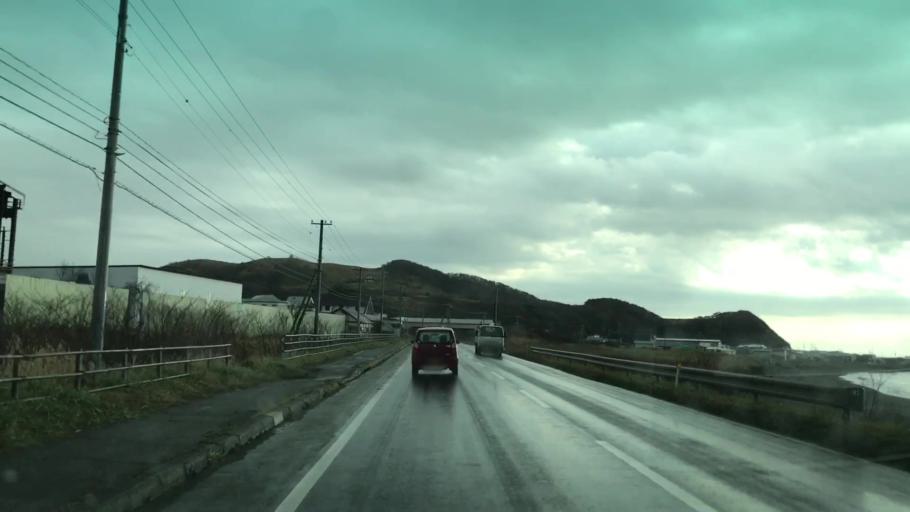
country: JP
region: Hokkaido
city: Shizunai-furukawacho
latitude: 42.1917
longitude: 142.6928
